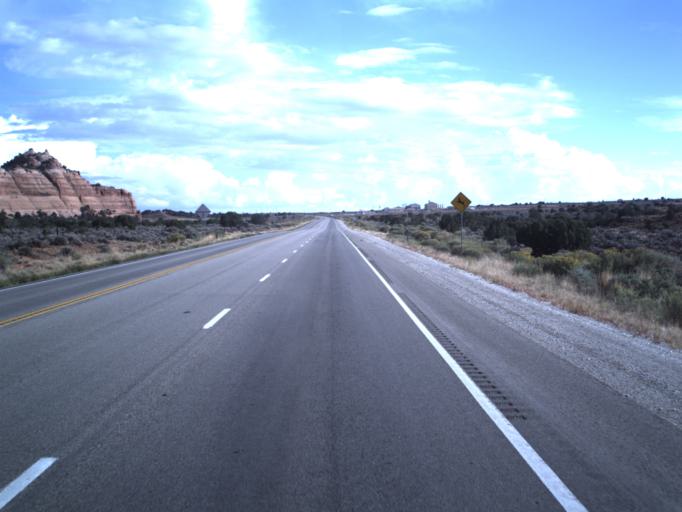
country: US
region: Utah
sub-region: Grand County
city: Moab
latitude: 38.3390
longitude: -109.4327
